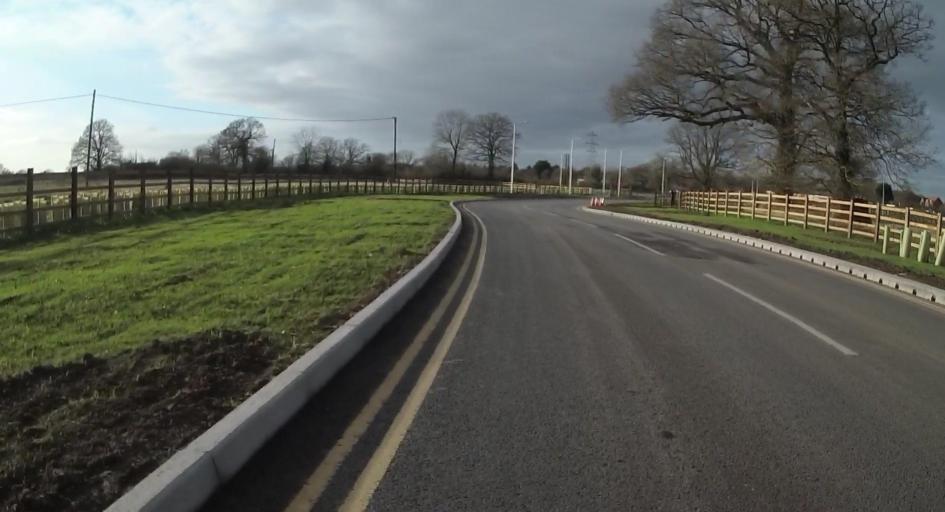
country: GB
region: England
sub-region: Wokingham
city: Wokingham
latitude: 51.4035
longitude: -0.8059
